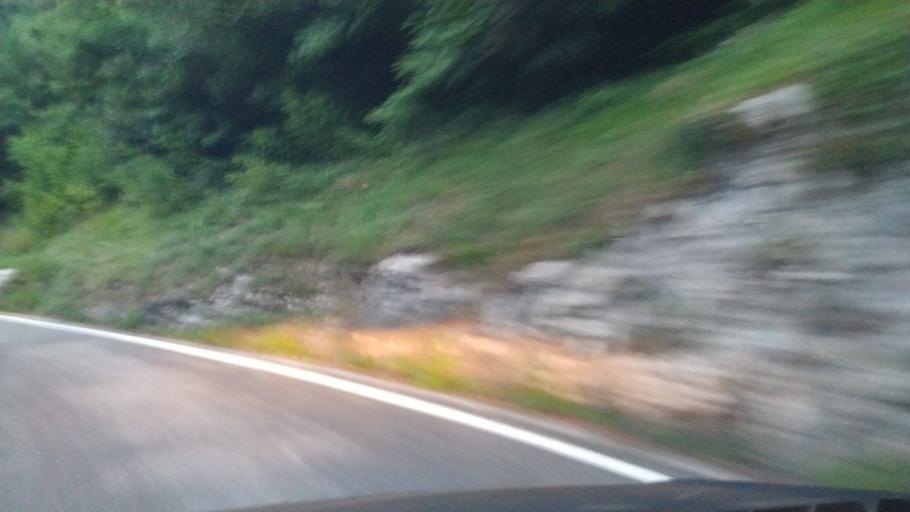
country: IT
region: Trentino-Alto Adige
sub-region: Provincia di Trento
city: Castelfondo
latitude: 46.4468
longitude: 11.1200
